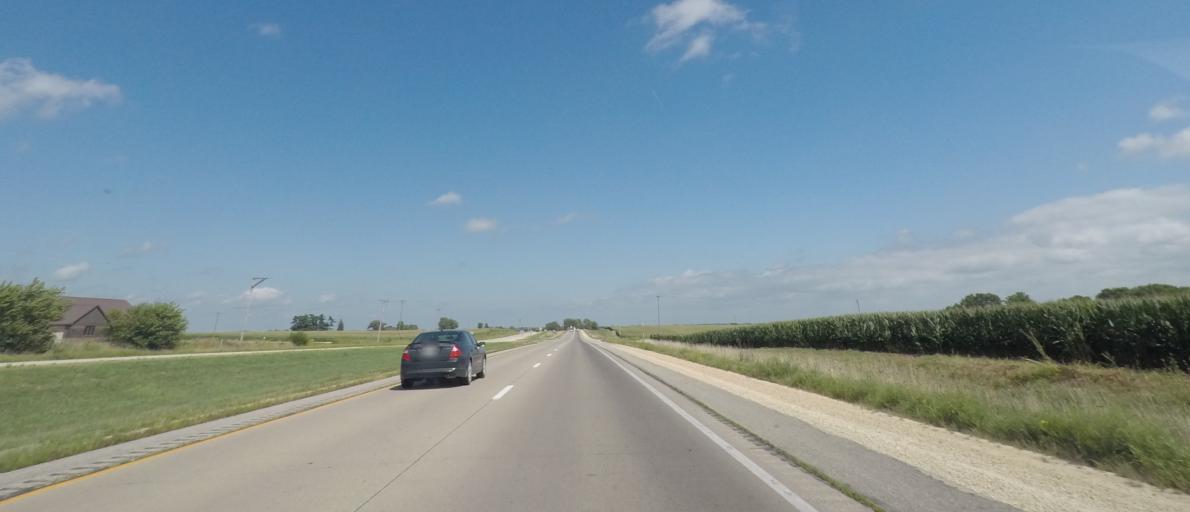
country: US
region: Iowa
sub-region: Linn County
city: Marion
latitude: 42.0393
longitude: -91.5232
